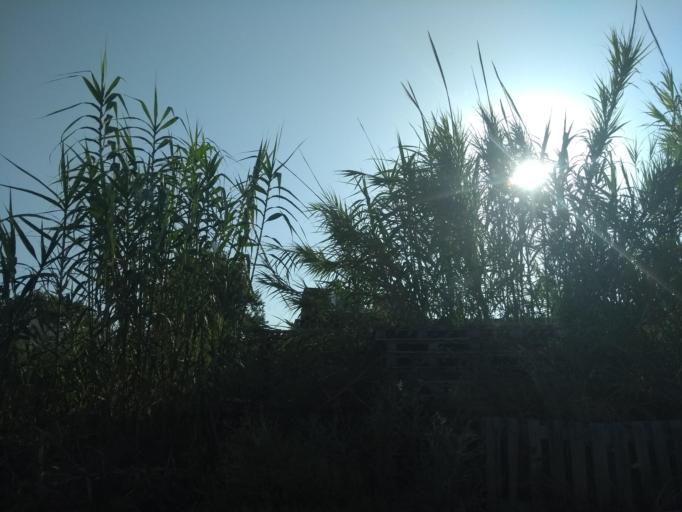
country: GR
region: Crete
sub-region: Nomos Chanias
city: Kalivai
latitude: 35.4510
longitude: 24.1742
